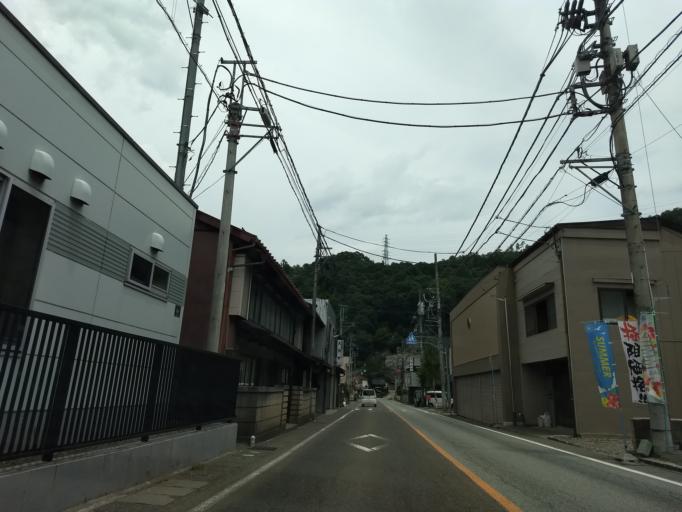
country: JP
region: Yamanashi
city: Otsuki
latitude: 35.5532
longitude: 138.9097
